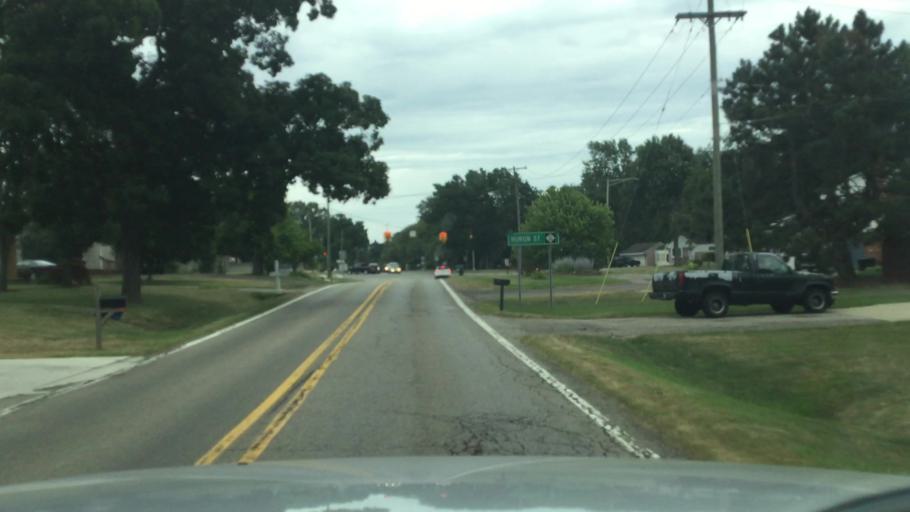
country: US
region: Michigan
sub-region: Oakland County
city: Sylvan Lake
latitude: 42.6360
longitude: -83.3408
